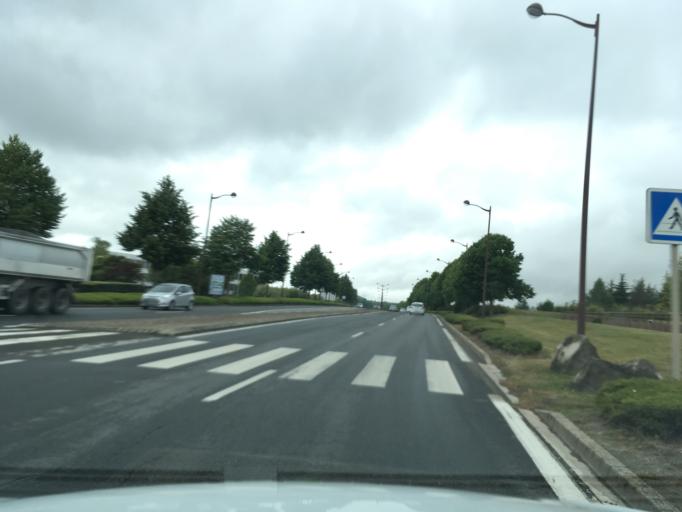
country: FR
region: Picardie
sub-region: Departement de l'Aisne
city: Saint-Quentin
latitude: 49.8555
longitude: 3.2612
